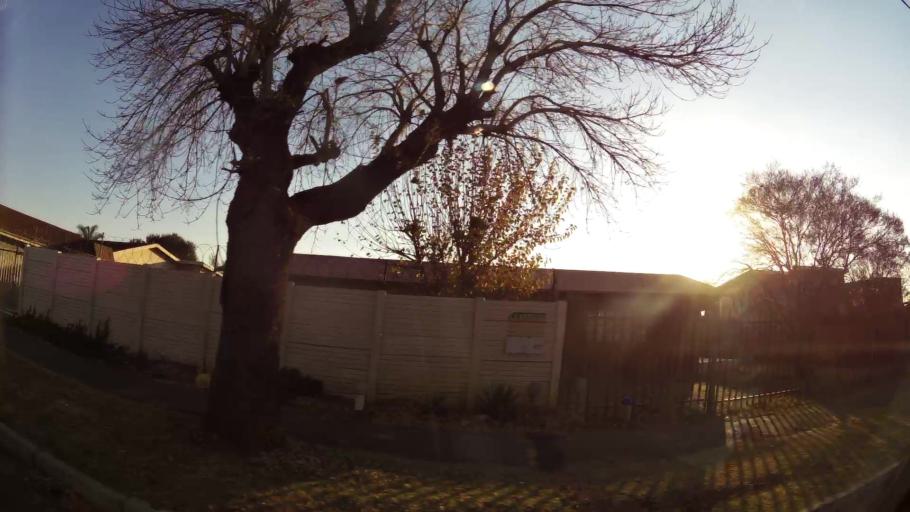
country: ZA
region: Gauteng
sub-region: City of Johannesburg Metropolitan Municipality
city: Johannesburg
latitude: -26.2541
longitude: 28.0072
